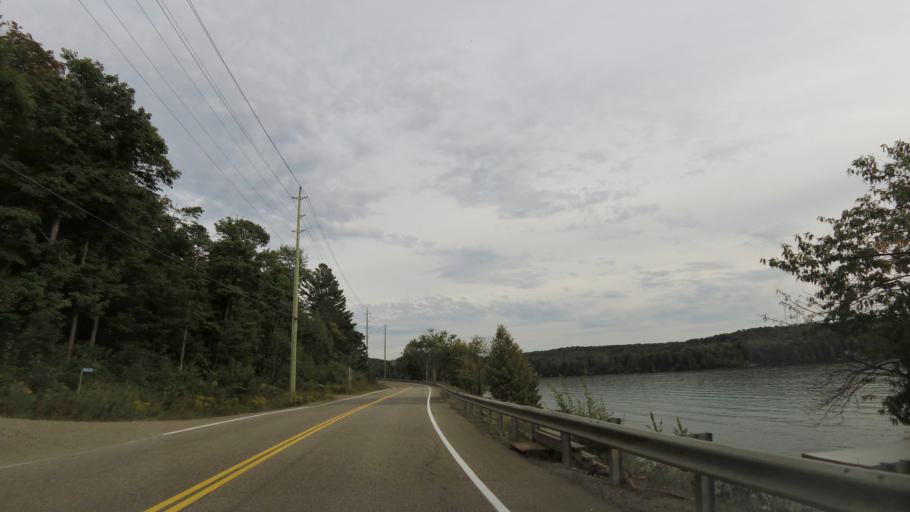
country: CA
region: Ontario
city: Bancroft
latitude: 45.0235
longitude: -78.3716
